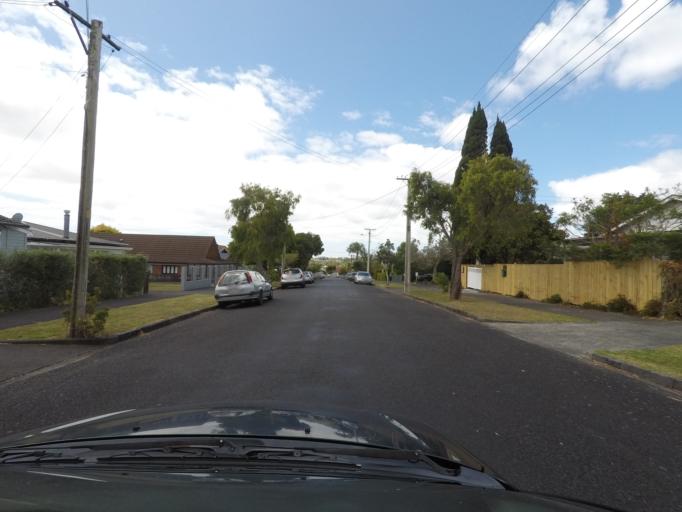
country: NZ
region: Auckland
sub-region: Auckland
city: Rosebank
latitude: -36.8675
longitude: 174.7063
